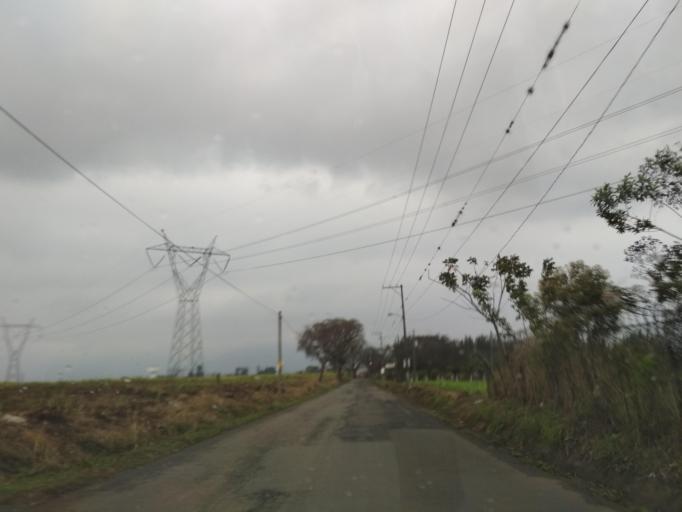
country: MX
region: Veracruz
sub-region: Cordoba
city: San Jose de Tapia
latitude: 18.8556
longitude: -96.9510
